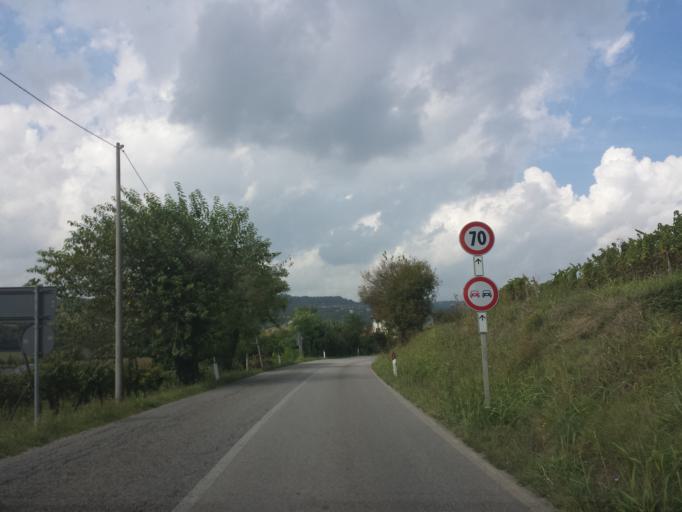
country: IT
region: Veneto
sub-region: Provincia di Vicenza
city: Sovizzo
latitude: 45.5335
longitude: 11.4412
